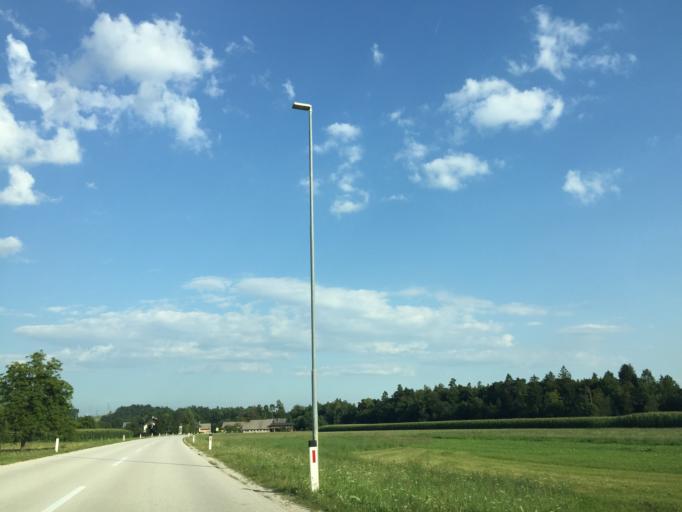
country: SI
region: Radovljica
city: Radovljica
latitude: 46.3224
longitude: 14.2249
